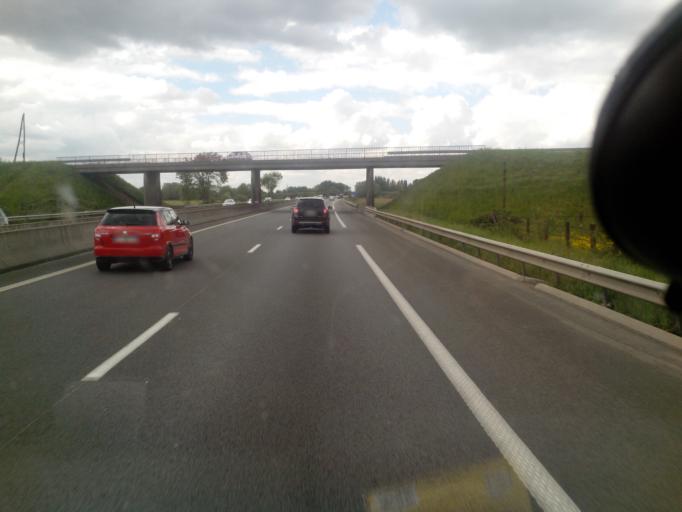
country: FR
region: Nord-Pas-de-Calais
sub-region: Departement du Nord
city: Steenwerck
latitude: 50.6968
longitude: 2.8024
